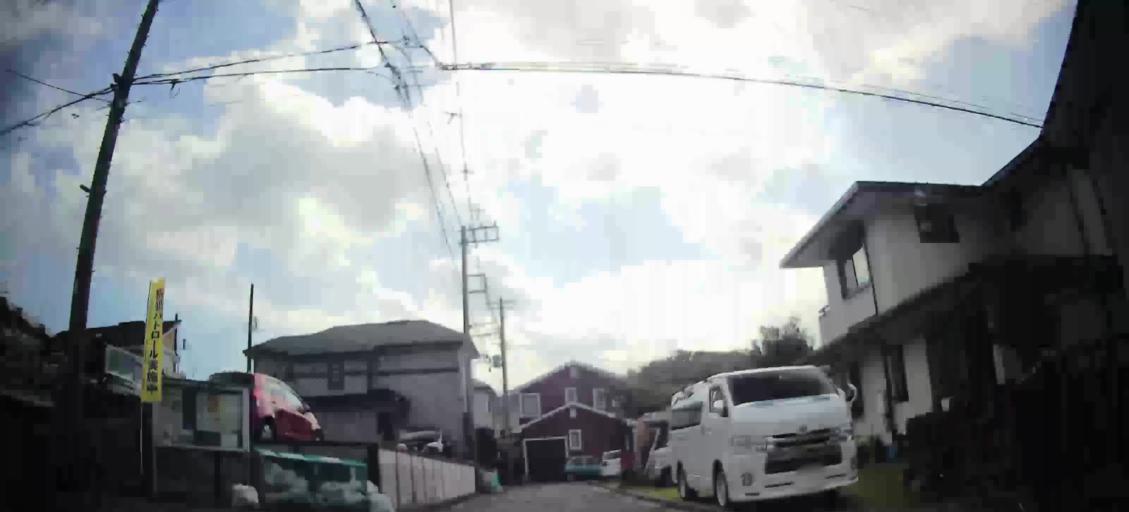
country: JP
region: Kanagawa
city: Yokohama
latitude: 35.4826
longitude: 139.5724
